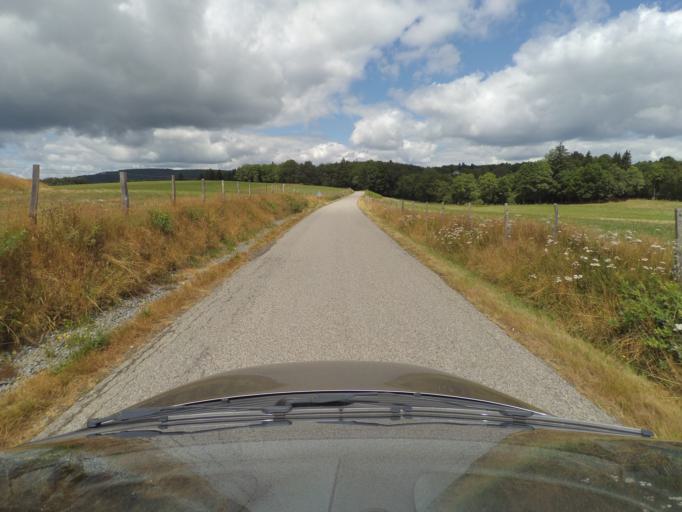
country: FR
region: Limousin
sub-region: Departement de la Creuse
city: Banize
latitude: 45.8147
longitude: 1.9313
